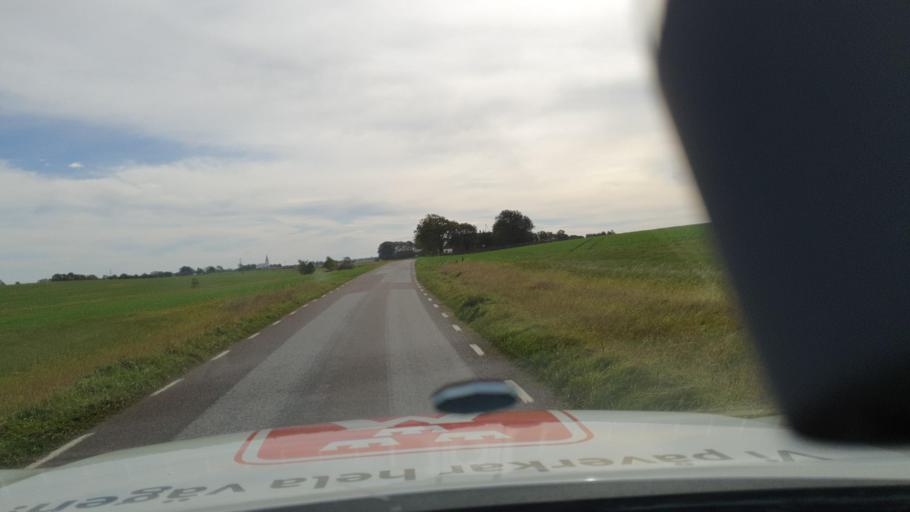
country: SE
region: Skane
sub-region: Vellinge Kommun
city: Vellinge
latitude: 55.4963
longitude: 13.0339
